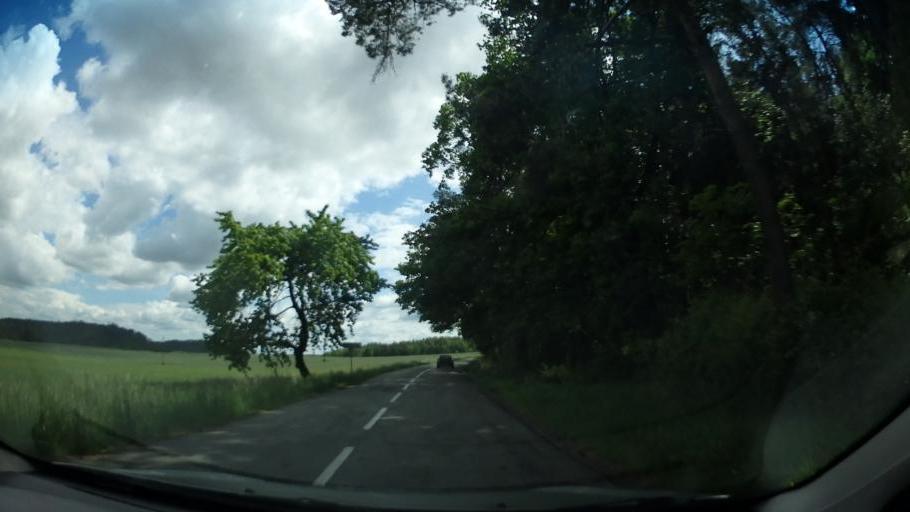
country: CZ
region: South Moravian
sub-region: Okres Blansko
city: Letovice
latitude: 49.6053
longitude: 16.6083
